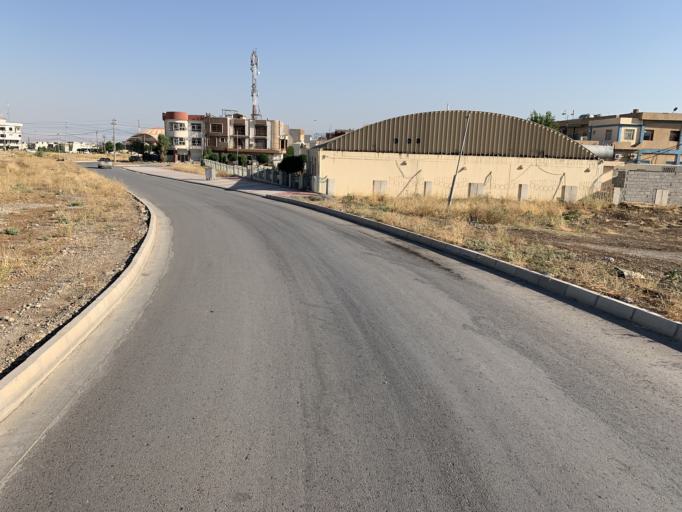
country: IQ
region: As Sulaymaniyah
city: Raniye
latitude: 36.2402
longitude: 44.8708
